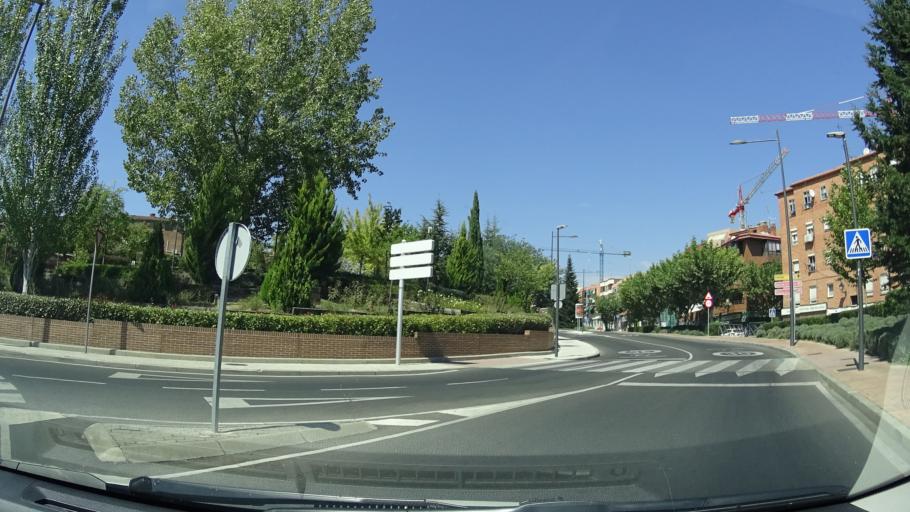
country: ES
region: Madrid
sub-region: Provincia de Madrid
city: Boadilla del Monte
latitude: 40.4039
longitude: -3.8774
